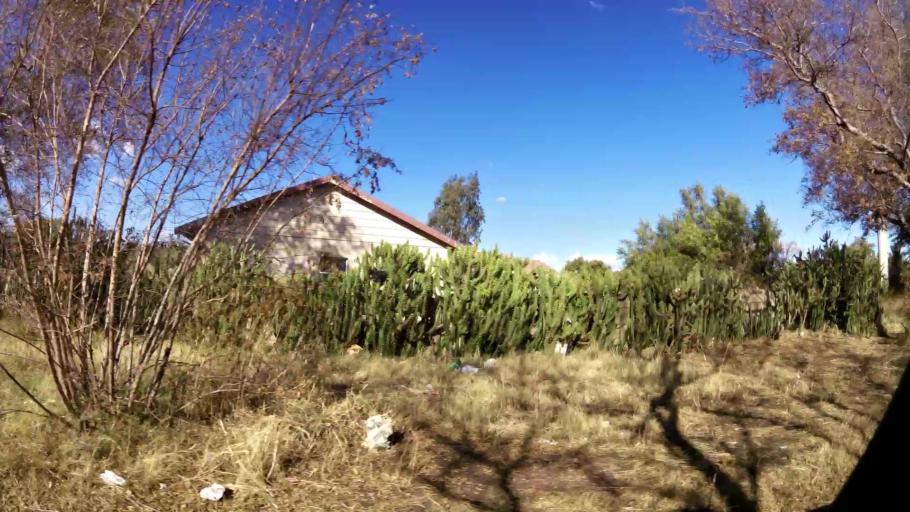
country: ZA
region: Gauteng
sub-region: West Rand District Municipality
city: Carletonville
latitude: -26.3613
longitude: 27.3700
